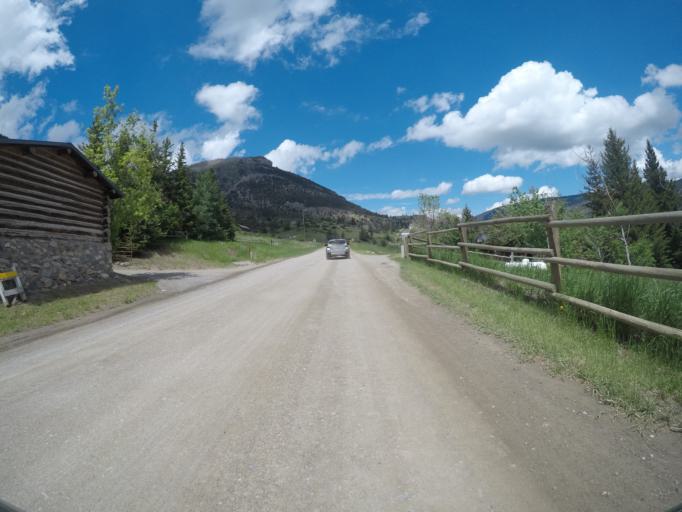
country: US
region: Montana
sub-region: Park County
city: Livingston
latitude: 45.5224
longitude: -110.2245
